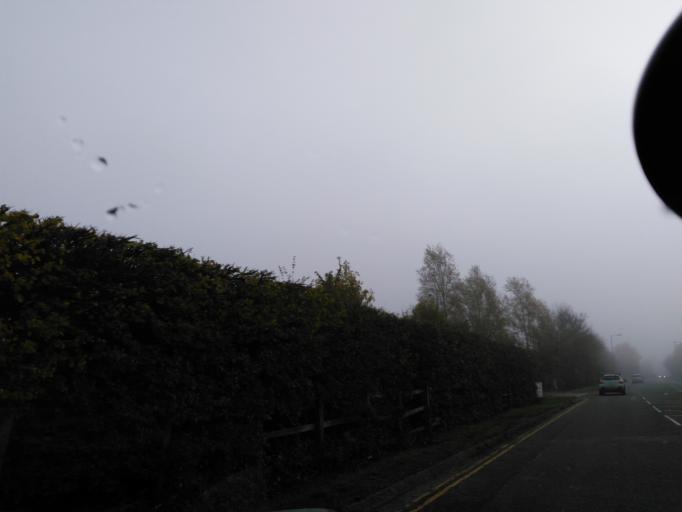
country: GB
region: England
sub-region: Wiltshire
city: Melksham
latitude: 51.3602
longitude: -2.1190
